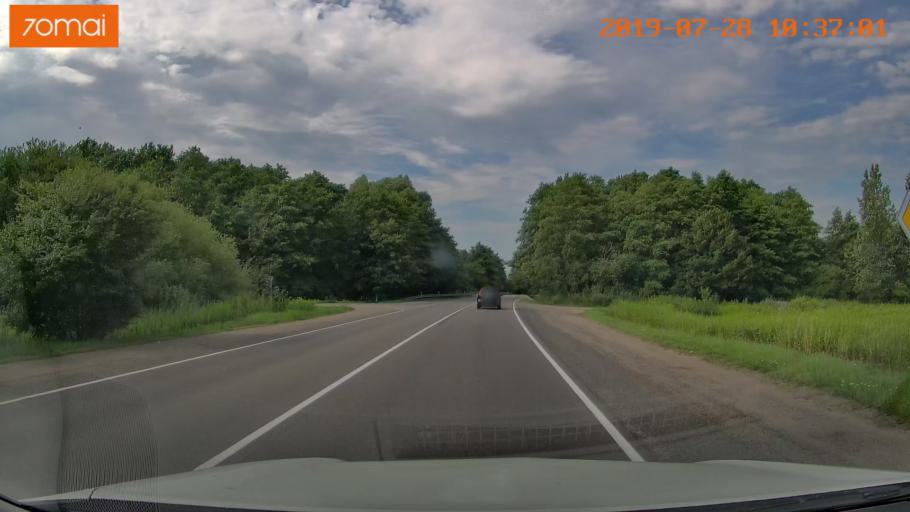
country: RU
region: Kaliningrad
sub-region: Gorod Kaliningrad
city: Kaliningrad
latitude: 54.7340
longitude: 20.4146
